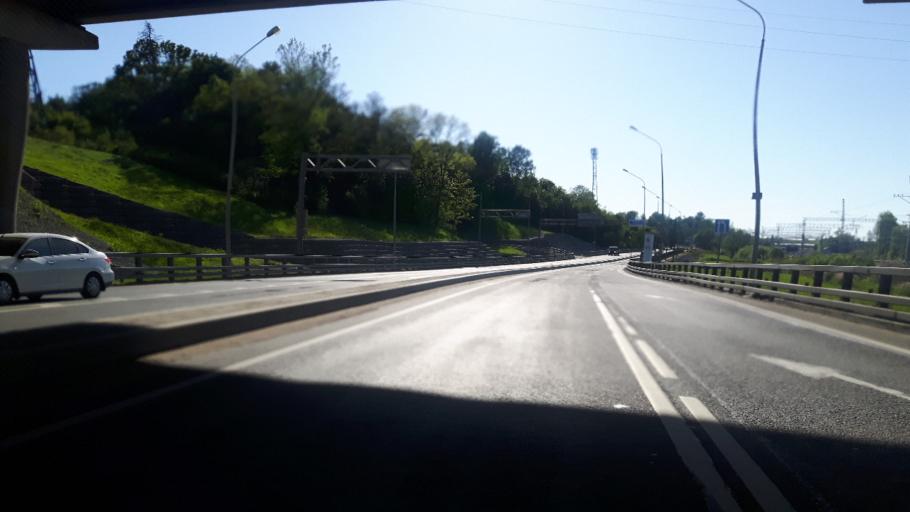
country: RU
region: St.-Petersburg
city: Bol'shaya Izhora
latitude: 59.9265
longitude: 29.6674
